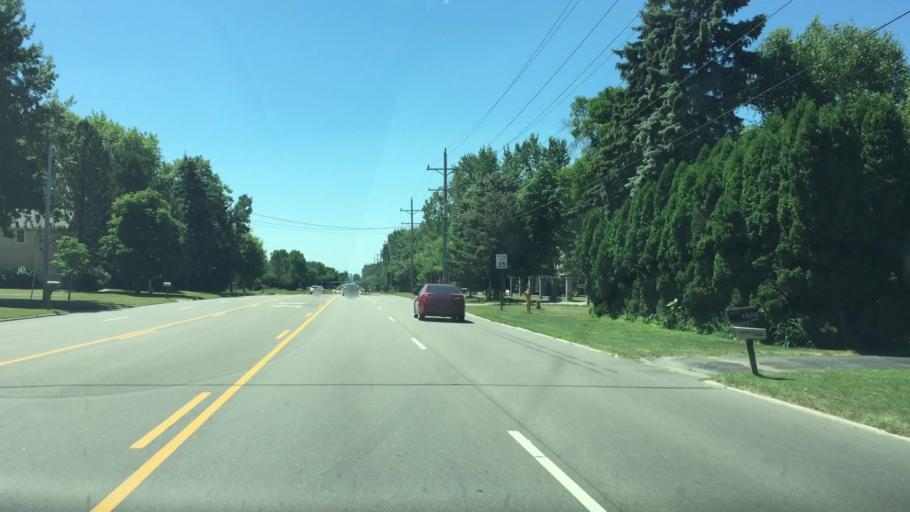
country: US
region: Wisconsin
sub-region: Outagamie County
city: Appleton
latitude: 44.2252
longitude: -88.4042
